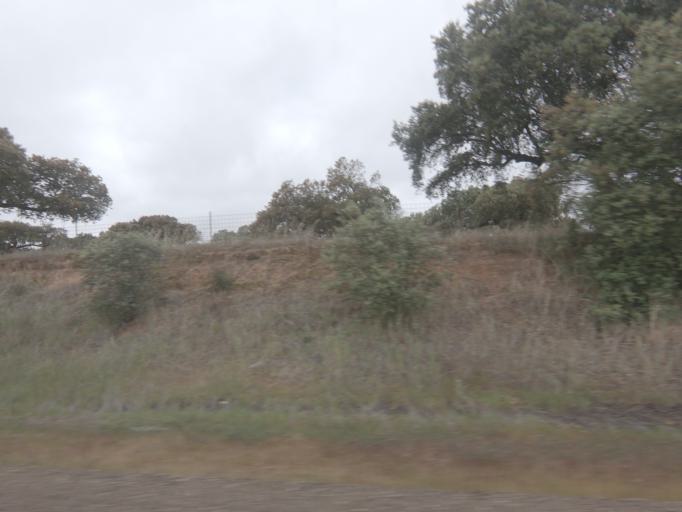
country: ES
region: Extremadura
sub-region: Provincia de Badajoz
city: Villar del Rey
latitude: 39.0305
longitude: -6.8321
